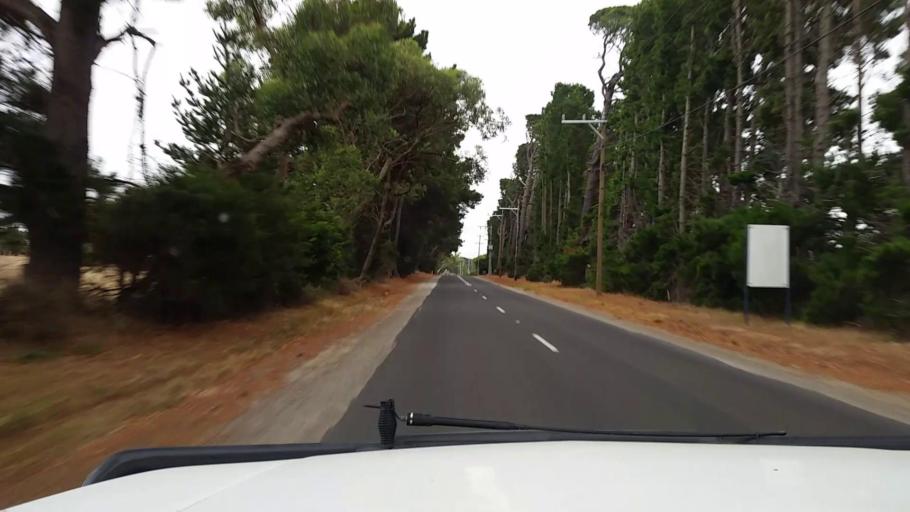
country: AU
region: Victoria
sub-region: Mornington Peninsula
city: Balnarring
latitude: -38.3365
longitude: 145.1457
